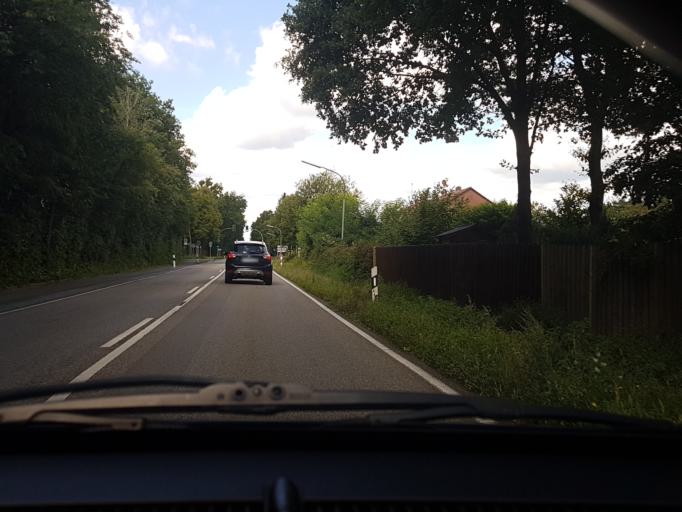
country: DE
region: North Rhine-Westphalia
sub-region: Regierungsbezirk Munster
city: Neuenkirchen
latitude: 52.2120
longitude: 7.3998
